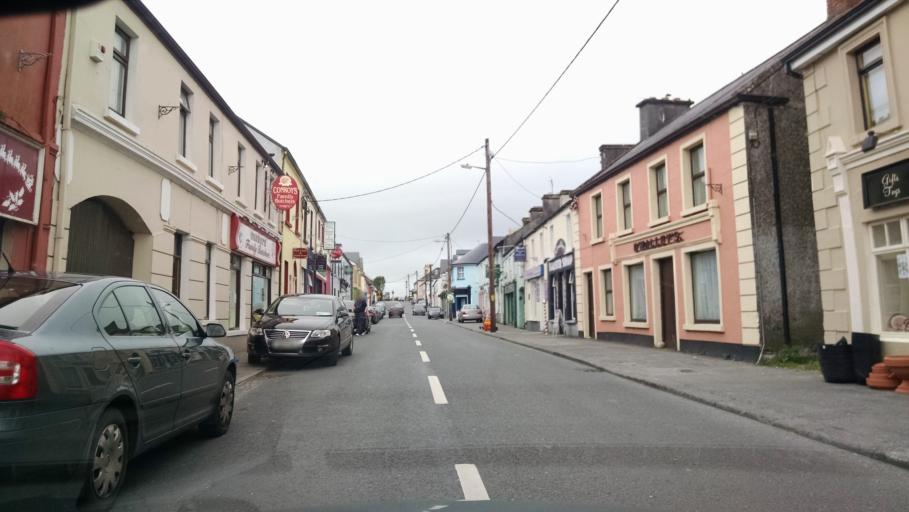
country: IE
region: Connaught
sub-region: County Galway
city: Moycullen
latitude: 53.4695
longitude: -9.1034
